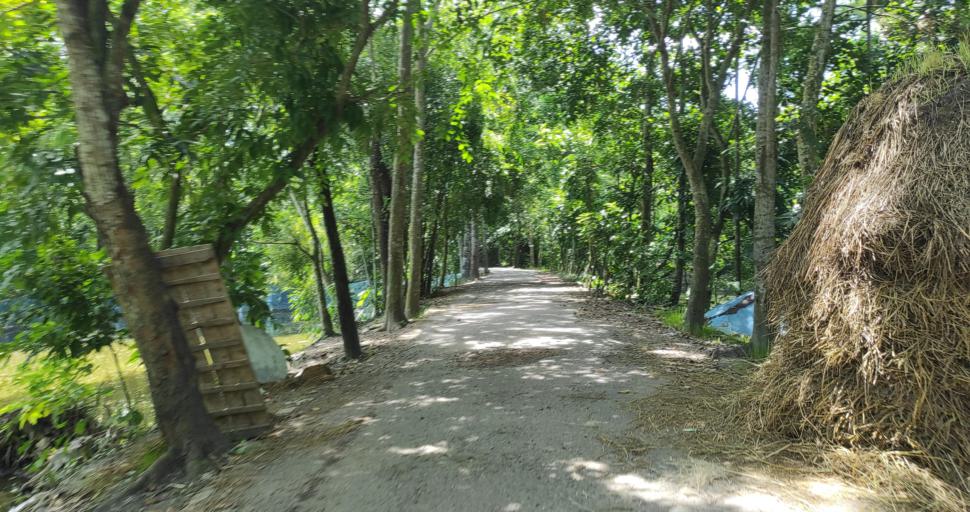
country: BD
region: Barisal
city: Gaurnadi
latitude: 22.9181
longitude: 90.0815
